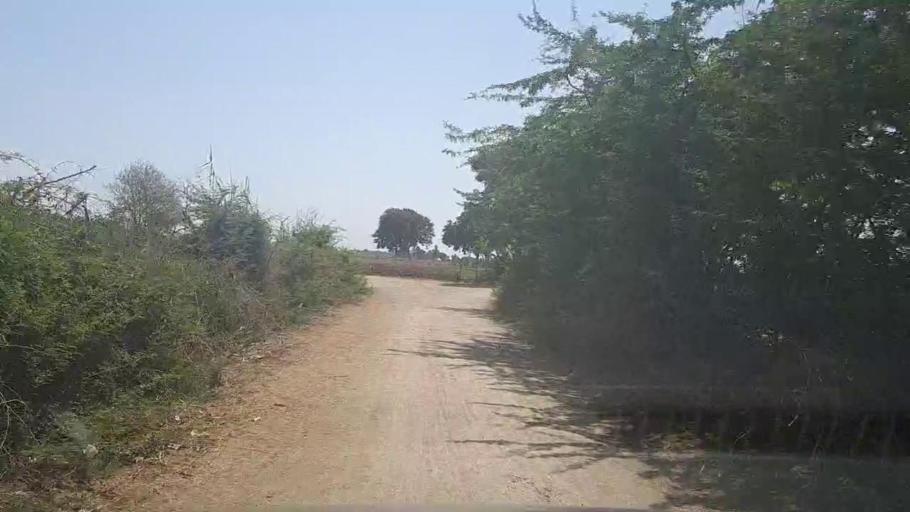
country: PK
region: Sindh
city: Thatta
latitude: 24.7886
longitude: 68.0124
